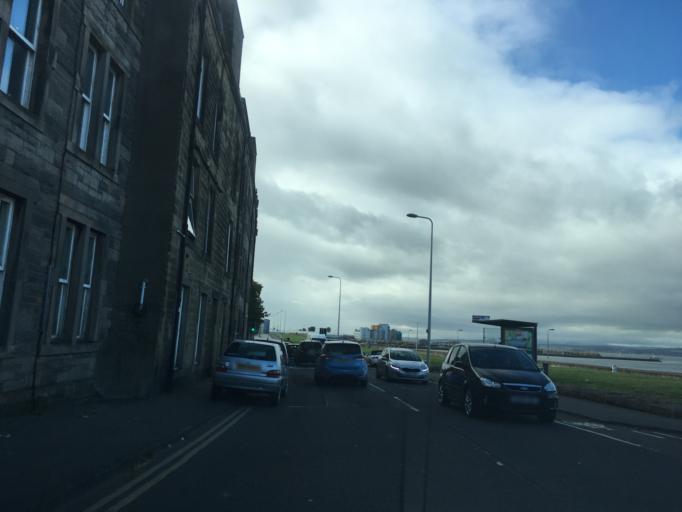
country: GB
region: Scotland
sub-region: Edinburgh
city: Edinburgh
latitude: 55.9799
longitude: -3.2071
